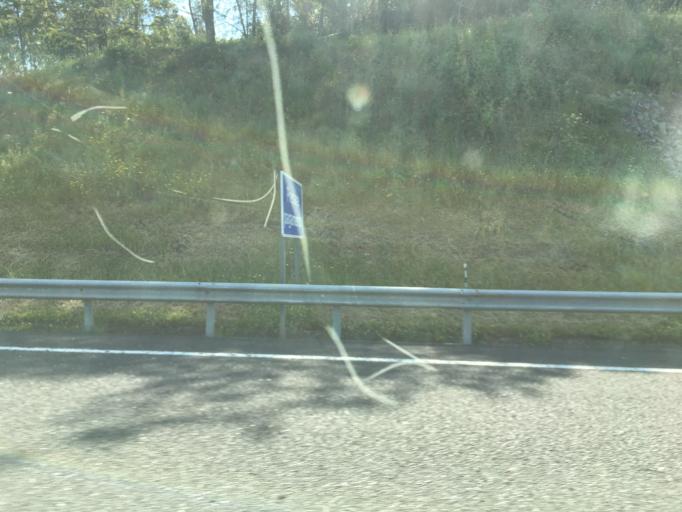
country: PT
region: Lisbon
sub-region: Sintra
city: Belas
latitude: 38.7874
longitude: -9.2403
